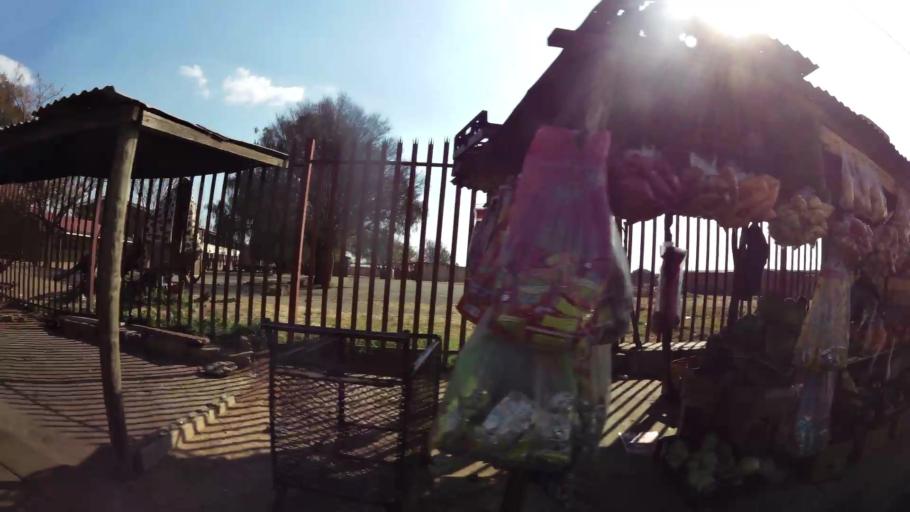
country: ZA
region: Gauteng
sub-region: Ekurhuleni Metropolitan Municipality
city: Brakpan
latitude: -26.1550
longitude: 28.4100
